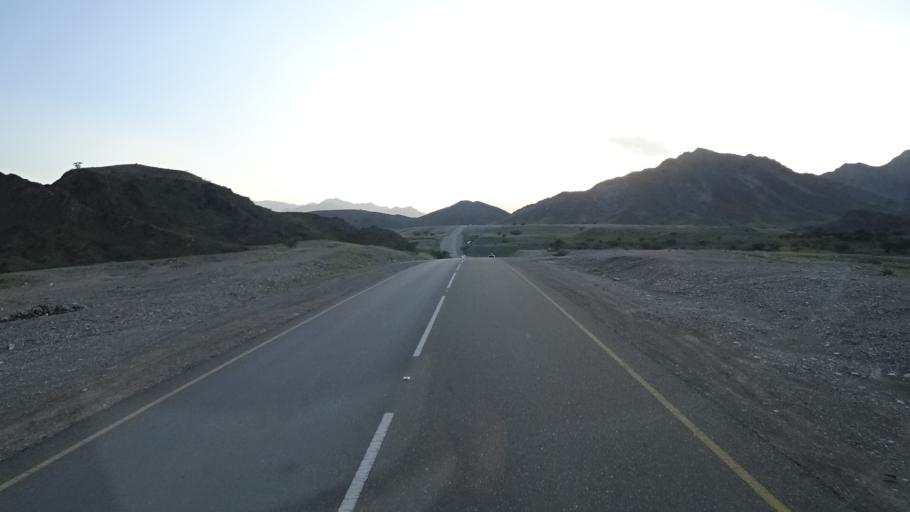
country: OM
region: Al Batinah
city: Al Khaburah
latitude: 23.8000
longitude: 56.9893
